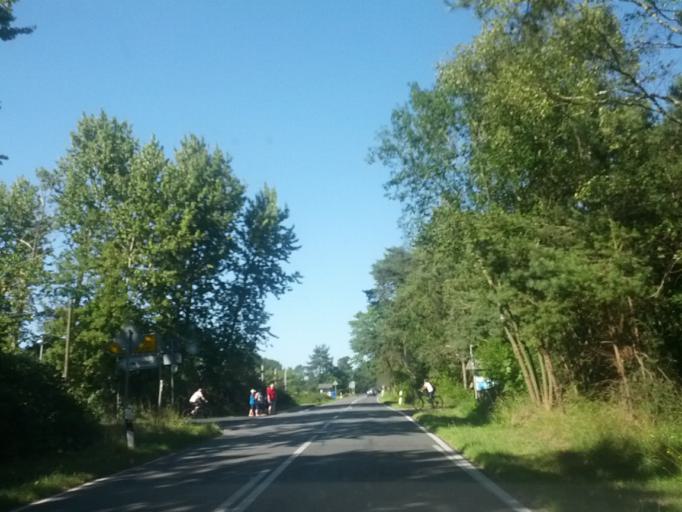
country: DE
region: Mecklenburg-Vorpommern
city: Ostseebad Gohren
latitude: 54.3024
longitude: 13.7143
